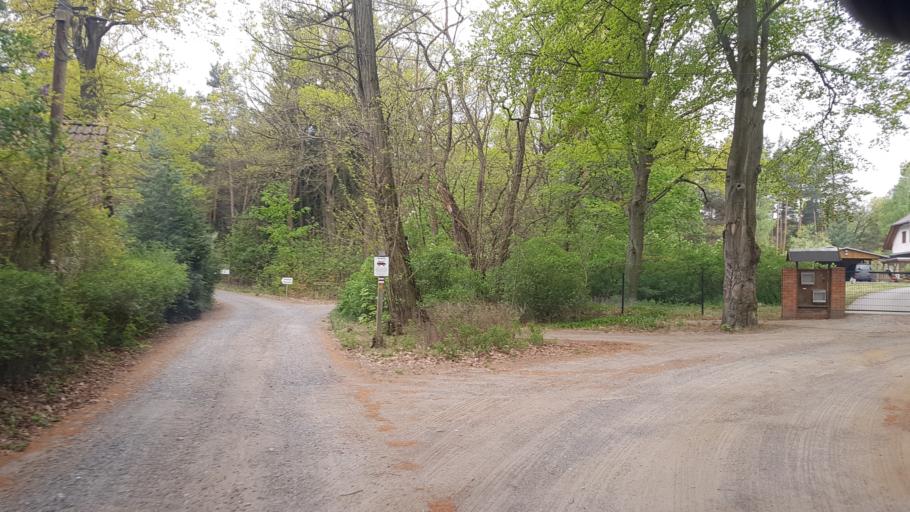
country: DE
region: Brandenburg
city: Altdobern
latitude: 51.6321
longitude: 14.0154
